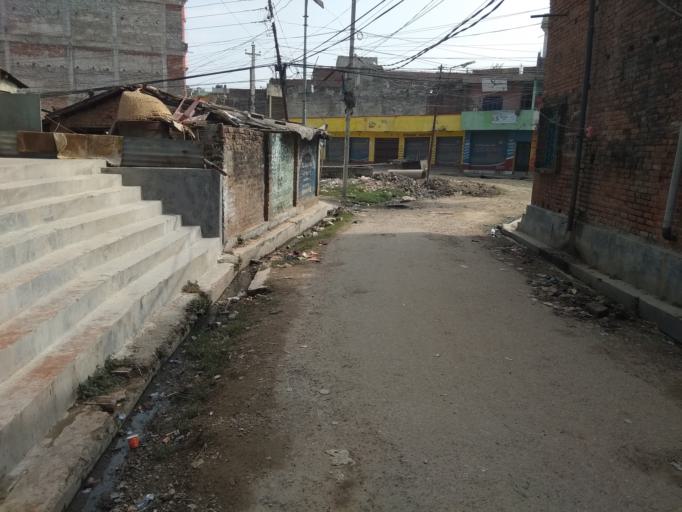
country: NP
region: Central Region
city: Janakpur
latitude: 26.7358
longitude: 85.9281
